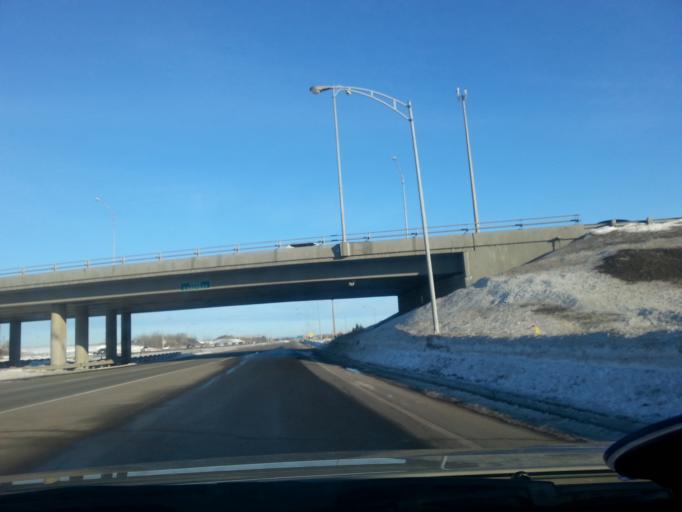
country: CA
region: Quebec
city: L'Ancienne-Lorette
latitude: 46.8225
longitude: -71.3649
